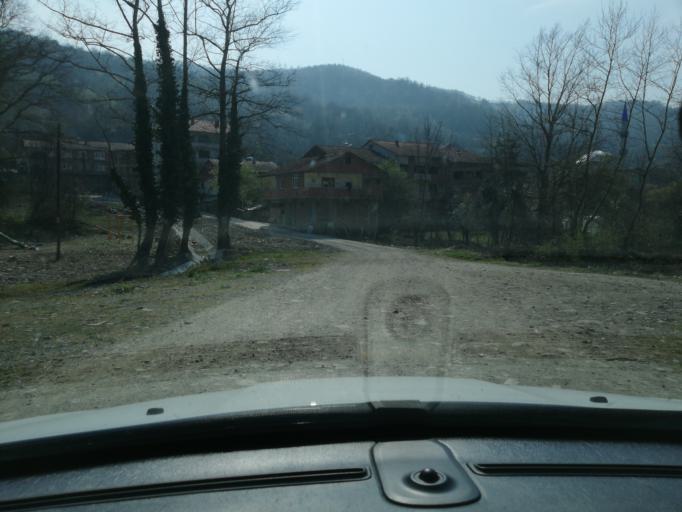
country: TR
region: Karabuk
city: Yenice
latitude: 41.2631
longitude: 32.3620
